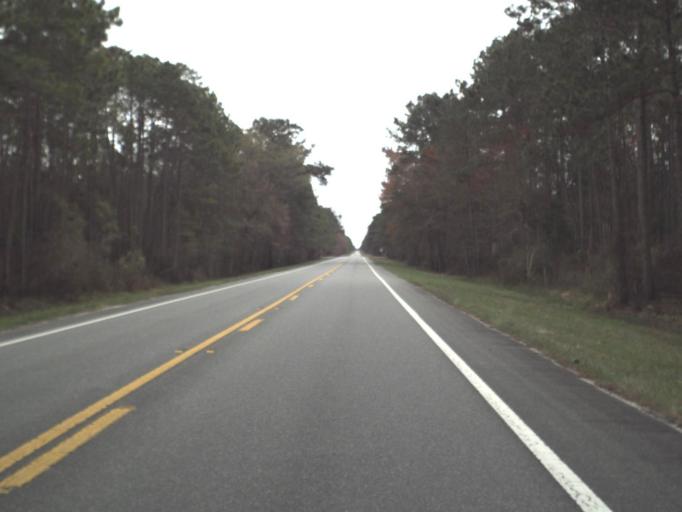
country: US
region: Florida
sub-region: Gadsden County
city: Midway
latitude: 30.3871
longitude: -84.5737
